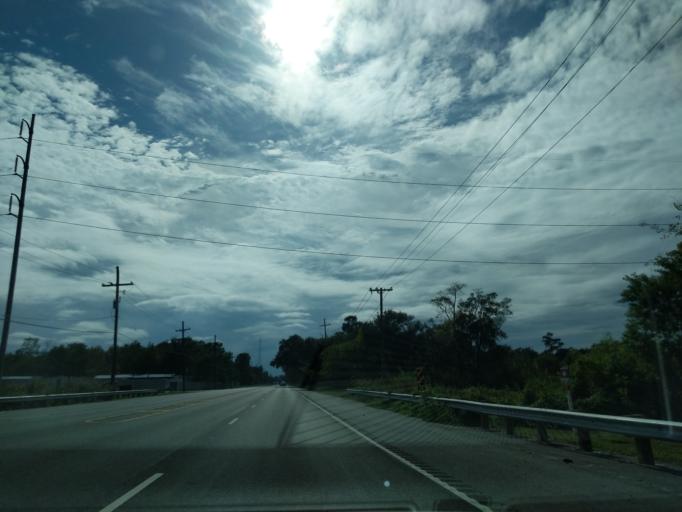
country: US
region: Louisiana
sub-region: Saint Bernard Parish
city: Meraux
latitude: 30.0525
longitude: -89.8799
